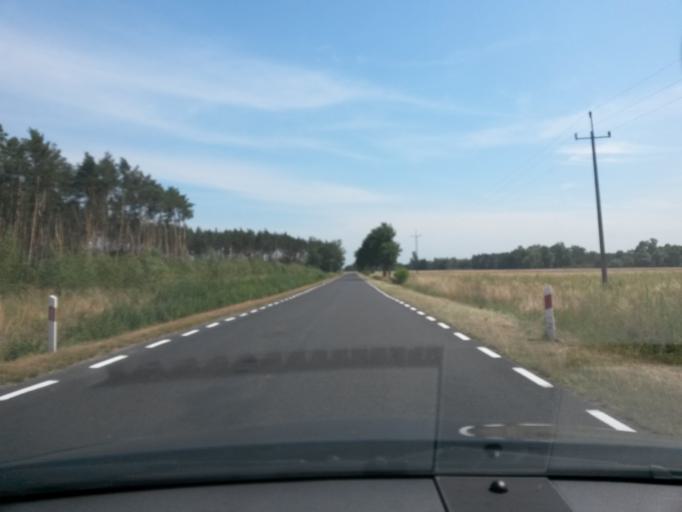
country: PL
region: Lower Silesian Voivodeship
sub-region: Powiat legnicki
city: Prochowice
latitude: 51.2932
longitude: 16.3720
